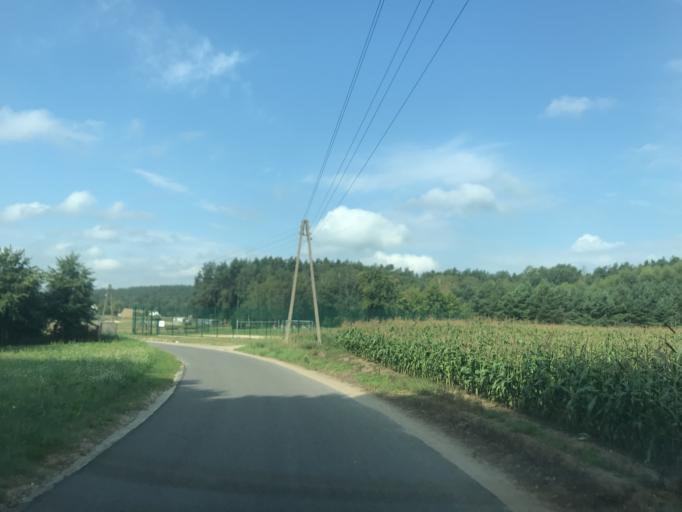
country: PL
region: Warmian-Masurian Voivodeship
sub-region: Powiat nowomiejski
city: Kurzetnik
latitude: 53.3536
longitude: 19.4973
